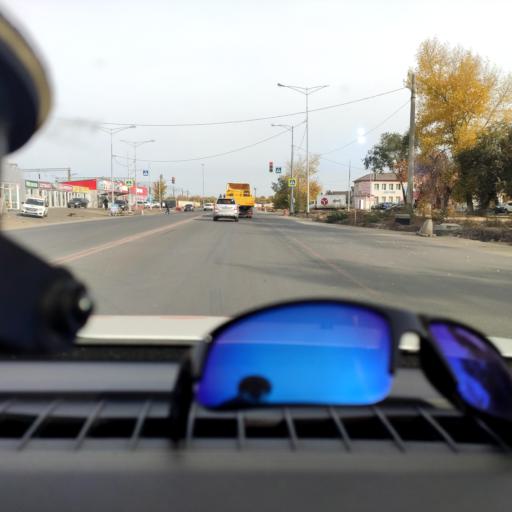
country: RU
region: Samara
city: Samara
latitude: 53.1261
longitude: 50.0898
